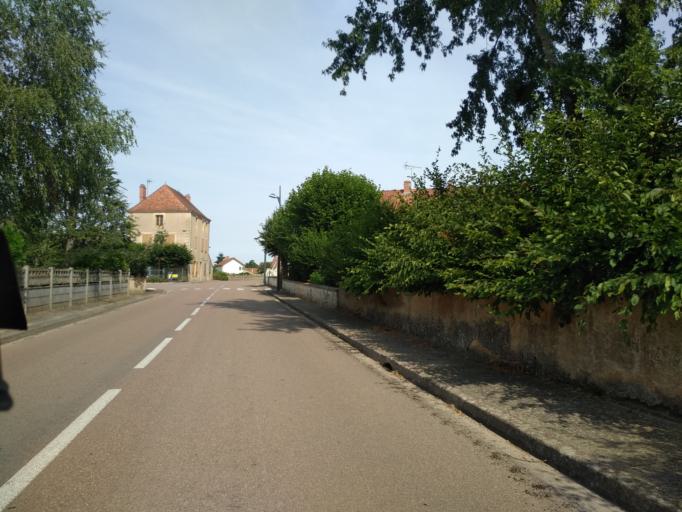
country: FR
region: Bourgogne
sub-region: Departement de Saone-et-Loire
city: Saint-Yan
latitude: 46.3526
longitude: 4.0117
